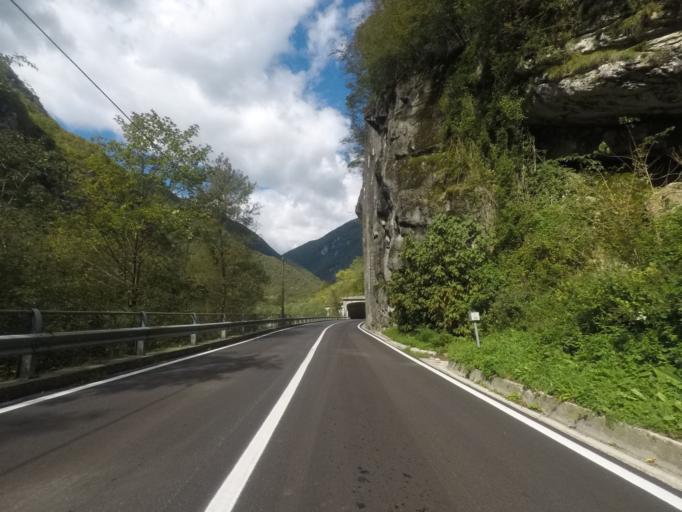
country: IT
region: Friuli Venezia Giulia
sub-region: Provincia di Udine
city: Pulfero
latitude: 46.1903
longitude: 13.4709
